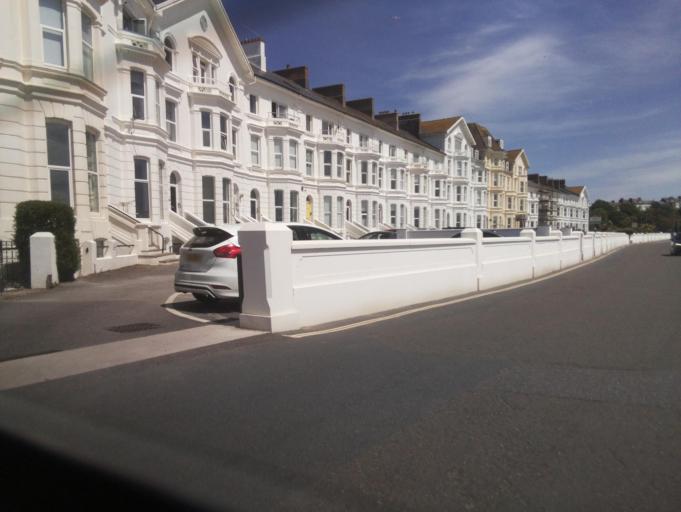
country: GB
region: England
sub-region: Devon
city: Exmouth
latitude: 50.6164
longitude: -3.4199
